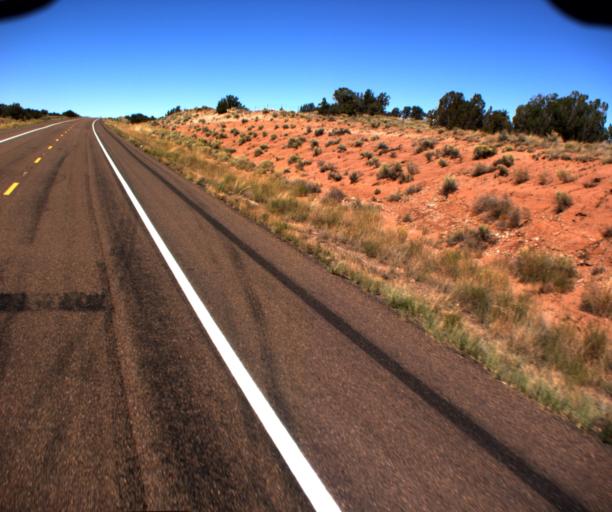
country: US
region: Arizona
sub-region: Apache County
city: Saint Johns
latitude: 34.6500
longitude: -109.7049
